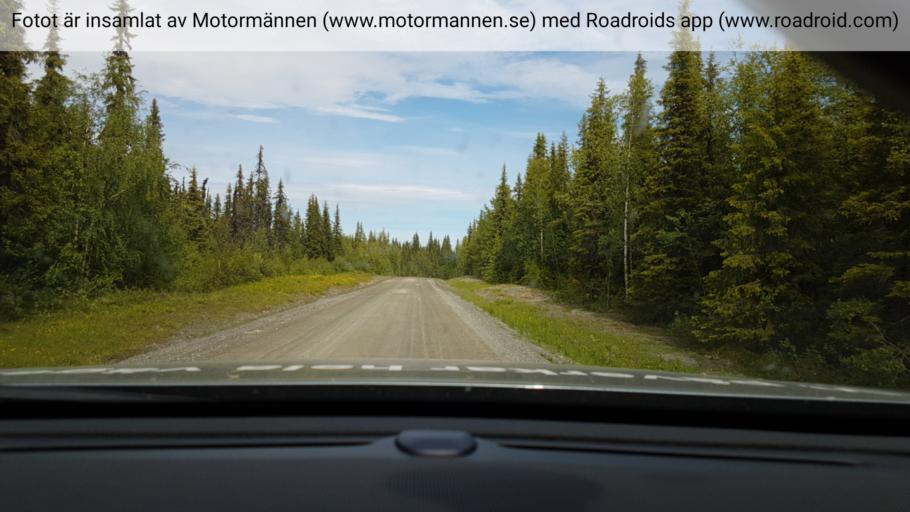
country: SE
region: Vaesterbotten
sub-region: Vilhelmina Kommun
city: Sjoberg
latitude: 65.1604
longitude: 16.3221
